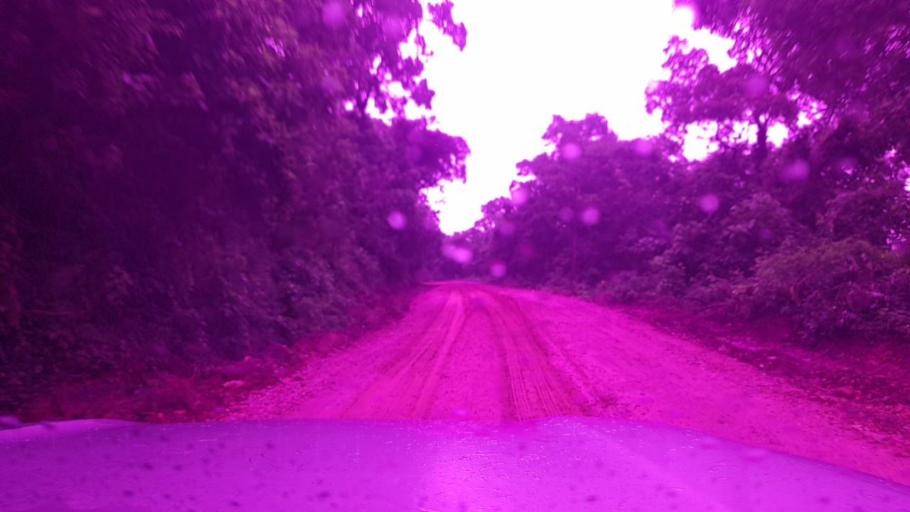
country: ET
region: Southern Nations, Nationalities, and People's Region
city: Bonga
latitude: 7.5033
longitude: 36.1014
